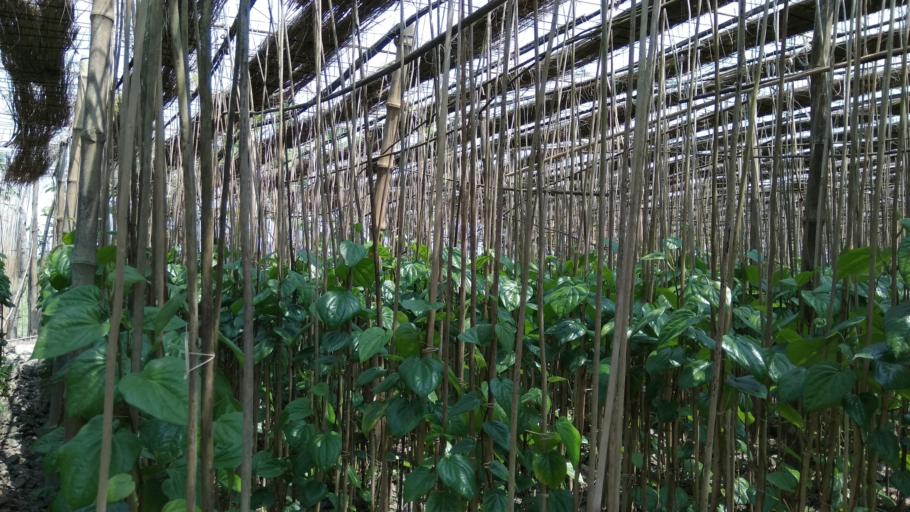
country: BD
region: Barisal
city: Gaurnadi
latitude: 22.9195
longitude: 90.3789
